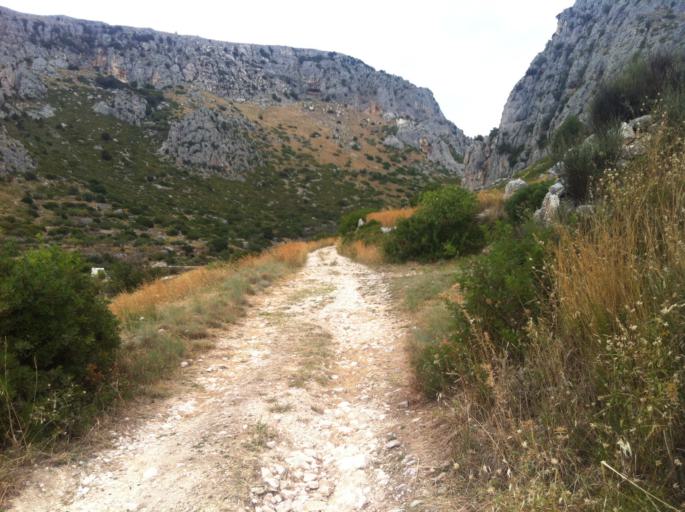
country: IT
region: Apulia
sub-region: Provincia di Foggia
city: Manfredonia
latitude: 41.6664
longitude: 15.9107
